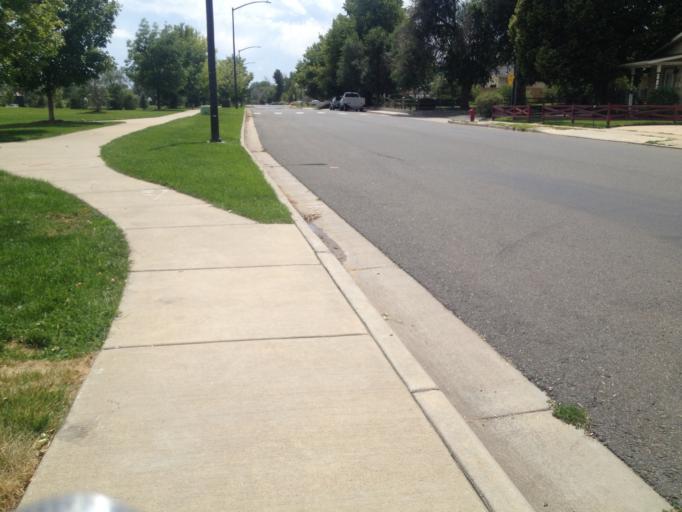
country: US
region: Colorado
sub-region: Boulder County
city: Louisville
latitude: 39.9723
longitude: -105.1327
